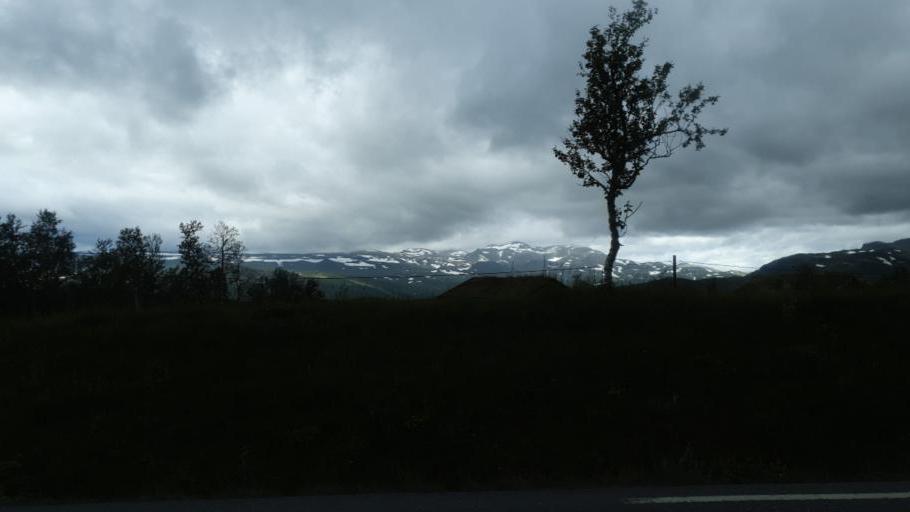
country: NO
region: Oppland
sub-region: Vestre Slidre
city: Slidre
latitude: 61.2614
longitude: 8.8739
